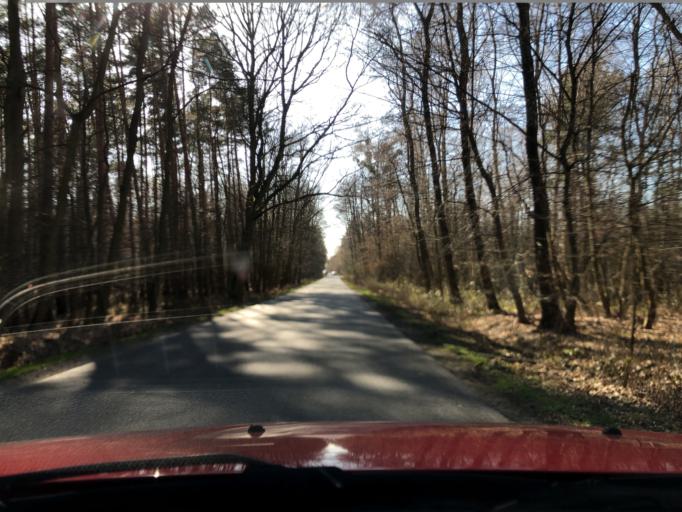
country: PL
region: Greater Poland Voivodeship
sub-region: Powiat pleszewski
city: Pleszew
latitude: 51.8546
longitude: 17.8250
